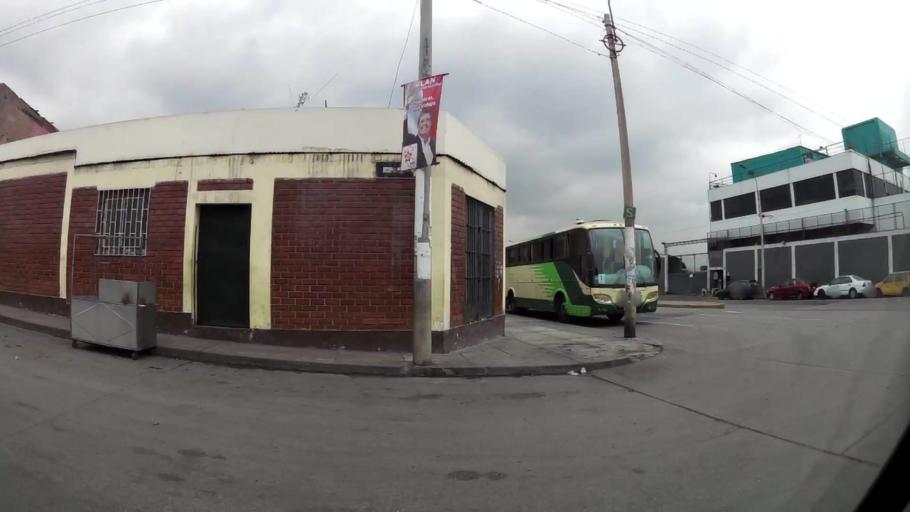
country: PE
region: Lima
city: Lima
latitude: -12.0410
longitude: -77.0414
